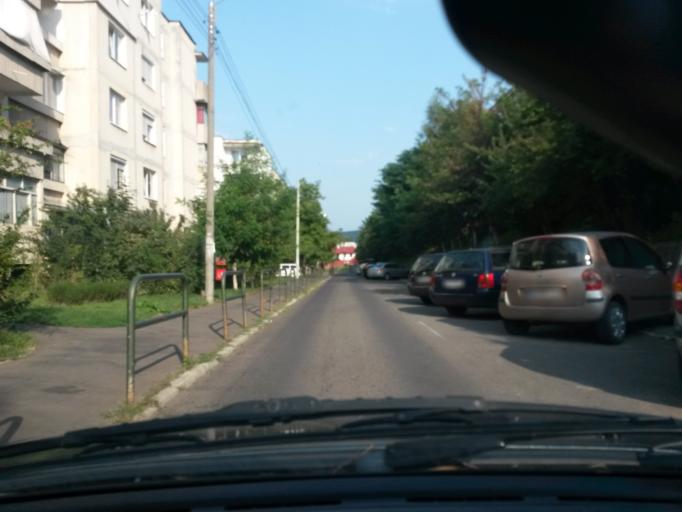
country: RO
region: Mures
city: Targu-Mures
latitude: 46.5315
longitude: 24.5804
